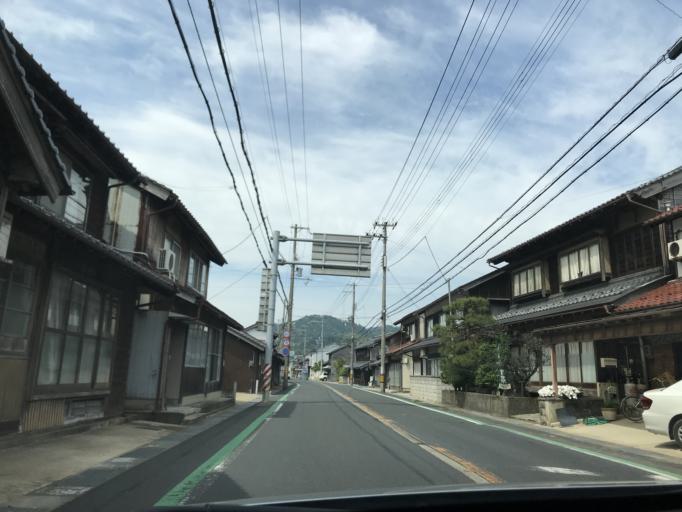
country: JP
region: Kyoto
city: Miyazu
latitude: 35.6797
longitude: 135.0303
